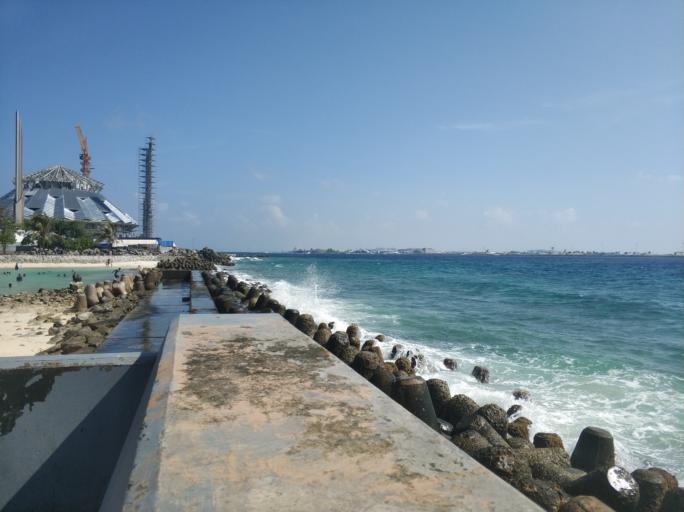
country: MV
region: Maale
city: Male
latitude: 4.1737
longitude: 73.5187
